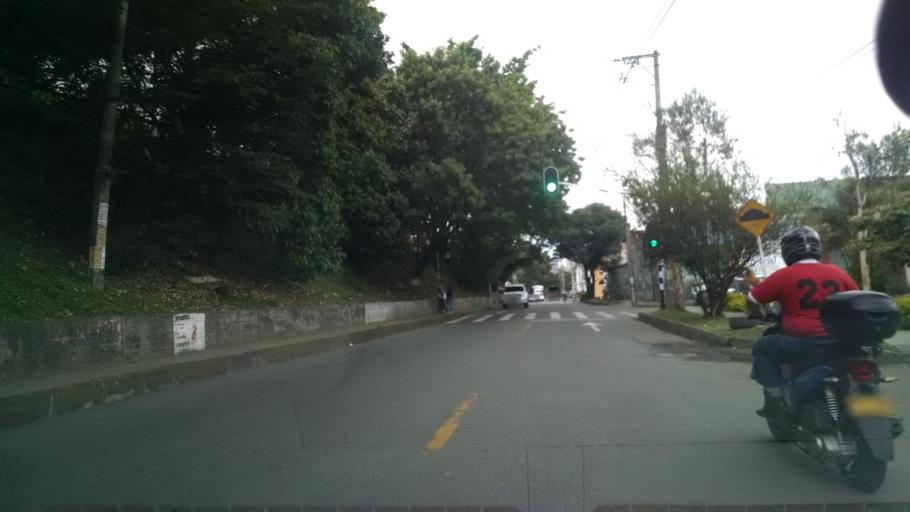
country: CO
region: Antioquia
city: Medellin
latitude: 6.2696
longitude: -75.5873
